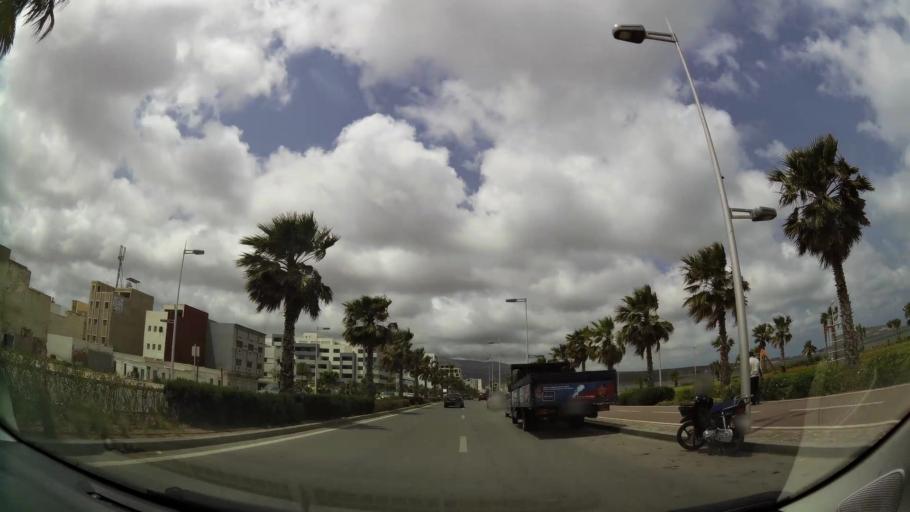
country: MA
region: Oriental
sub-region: Nador
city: Nador
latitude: 35.1764
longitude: -2.9194
